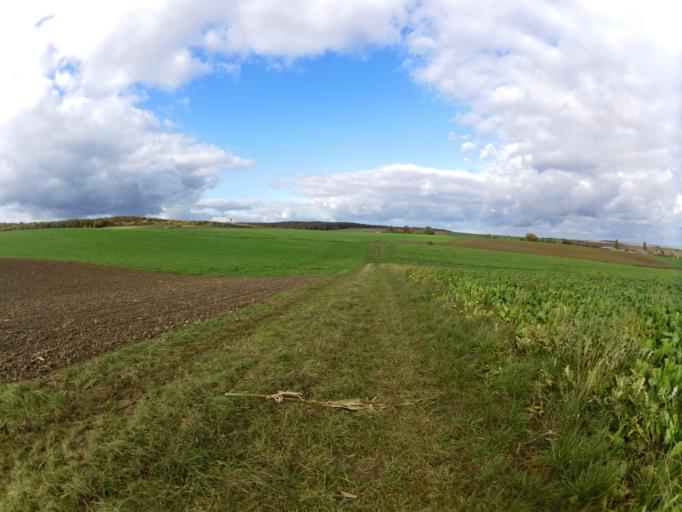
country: DE
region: Bavaria
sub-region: Regierungsbezirk Unterfranken
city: Unterpleichfeld
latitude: 49.8782
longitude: 10.0078
